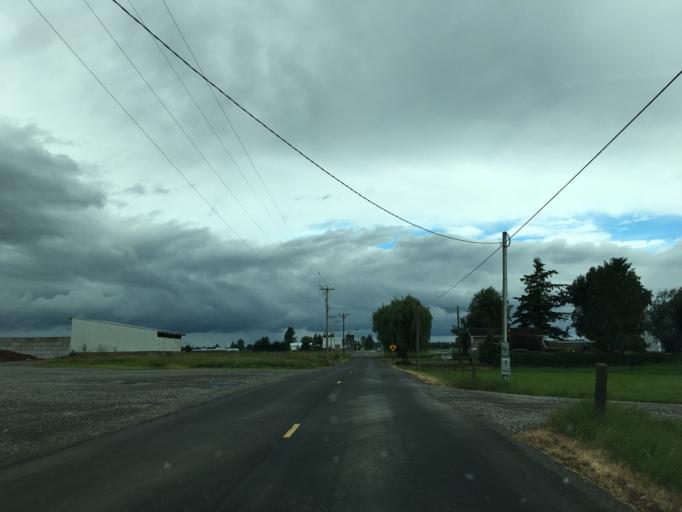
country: US
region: Washington
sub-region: Whatcom County
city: Sumas
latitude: 48.9748
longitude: -122.2687
